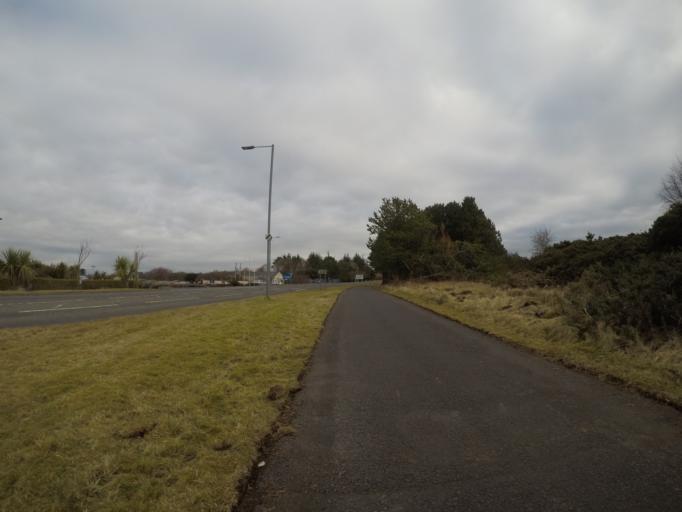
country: GB
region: Scotland
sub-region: North Ayrshire
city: Irvine
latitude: 55.5924
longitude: -4.6562
